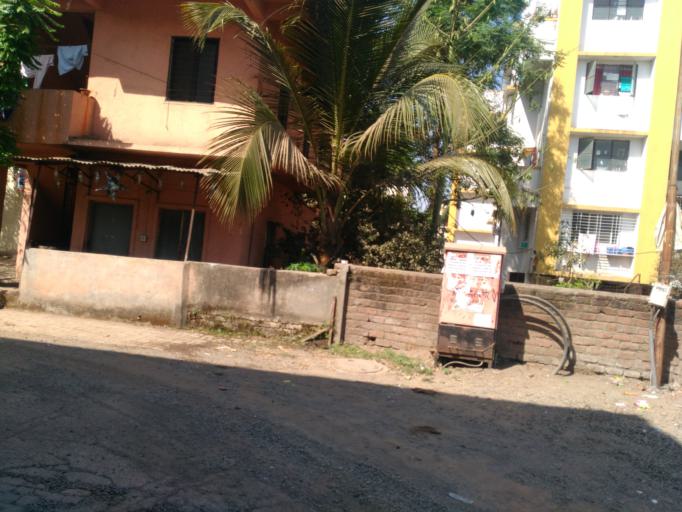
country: IN
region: Maharashtra
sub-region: Pune Division
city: Pune
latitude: 18.4480
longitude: 73.8767
